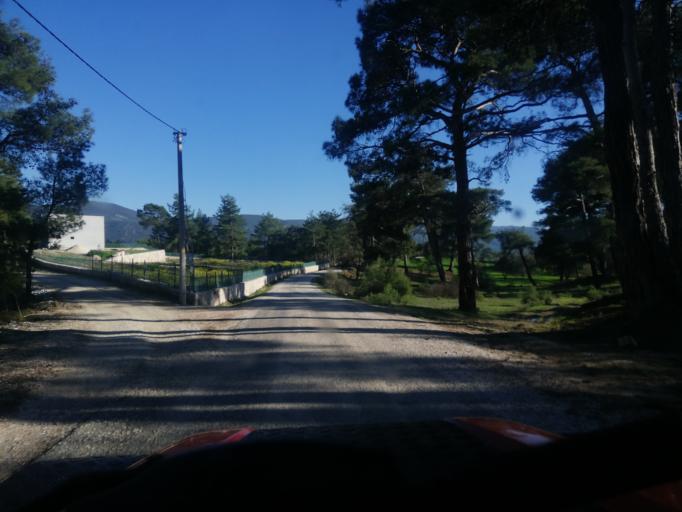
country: TR
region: Antalya
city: Kas
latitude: 36.2976
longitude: 29.7047
